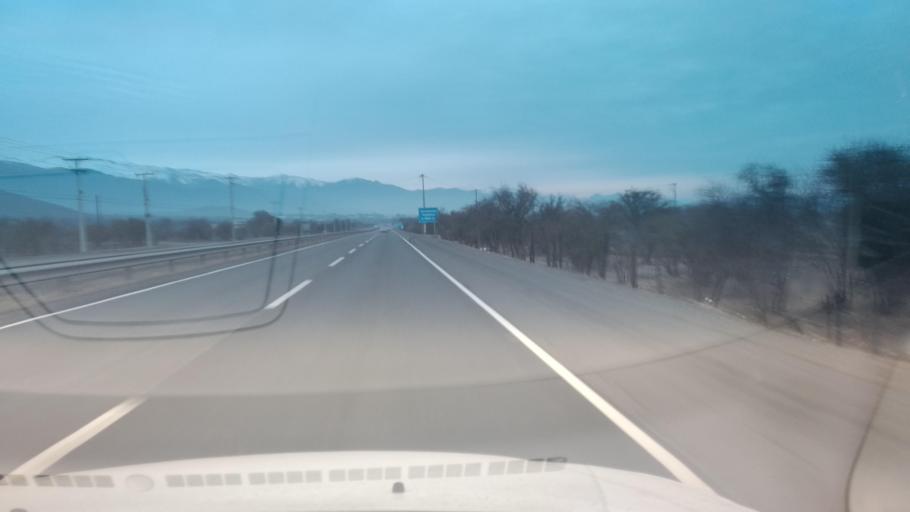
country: CL
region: Santiago Metropolitan
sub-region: Provincia de Chacabuco
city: Chicureo Abajo
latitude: -33.1175
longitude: -70.6817
